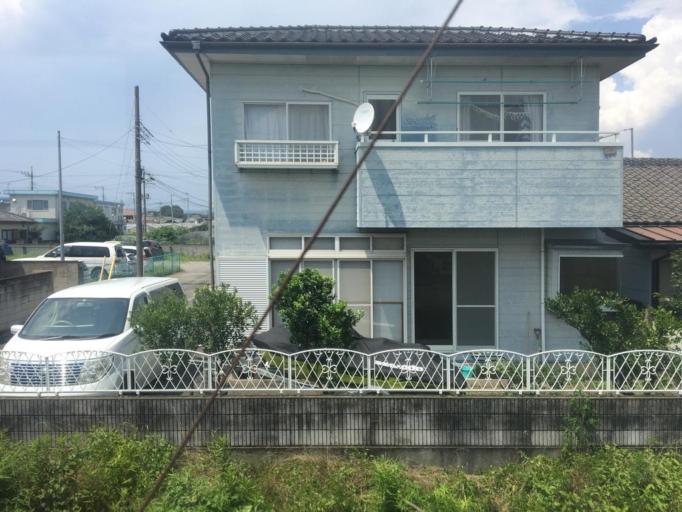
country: JP
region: Gunma
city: Maebashi-shi
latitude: 36.3941
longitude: 139.1083
